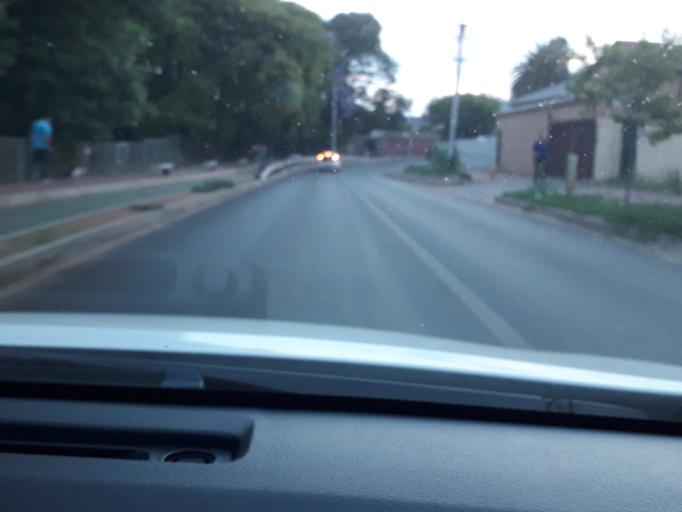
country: ZA
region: Gauteng
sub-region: City of Johannesburg Metropolitan Municipality
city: Johannesburg
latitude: -26.1790
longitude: 27.9900
